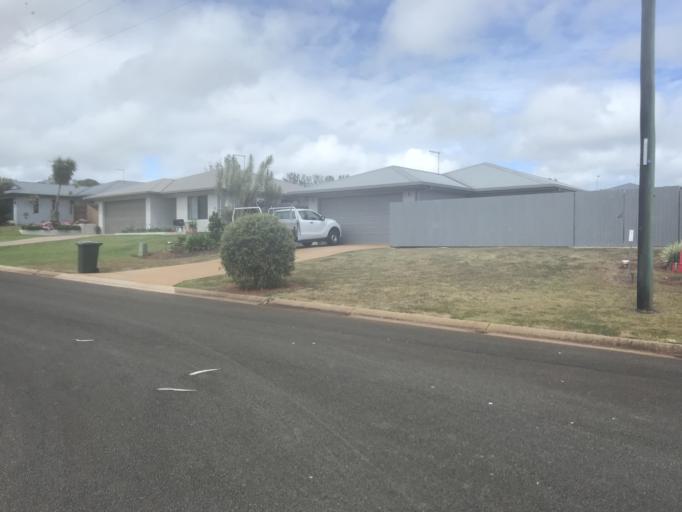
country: AU
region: Queensland
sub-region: Tablelands
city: Tolga
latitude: -17.2216
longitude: 145.4761
